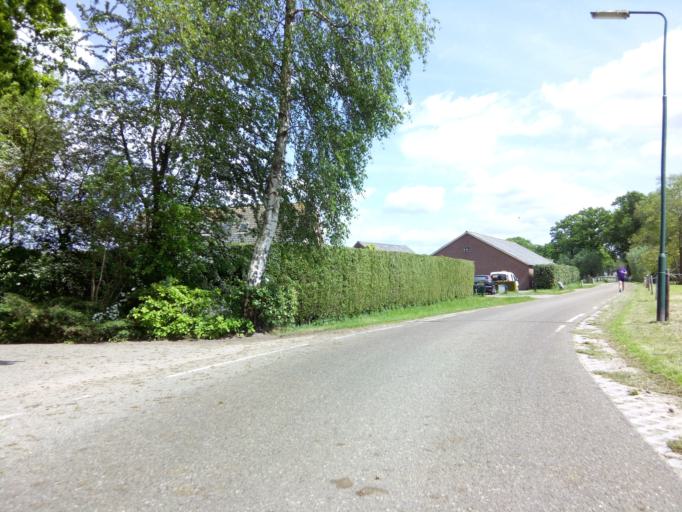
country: NL
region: Utrecht
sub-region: Gemeente Woudenberg
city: Woudenberg
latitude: 52.0756
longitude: 5.4587
